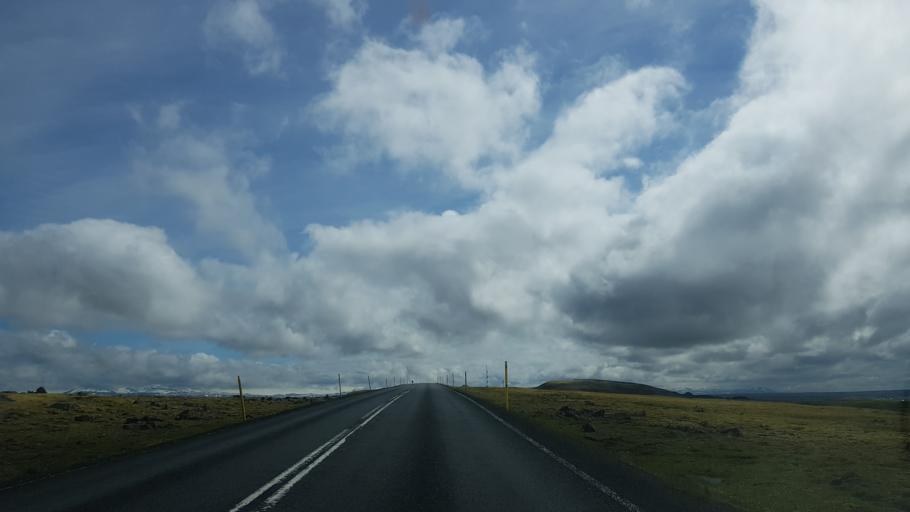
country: IS
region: West
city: Borgarnes
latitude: 64.9927
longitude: -21.0612
